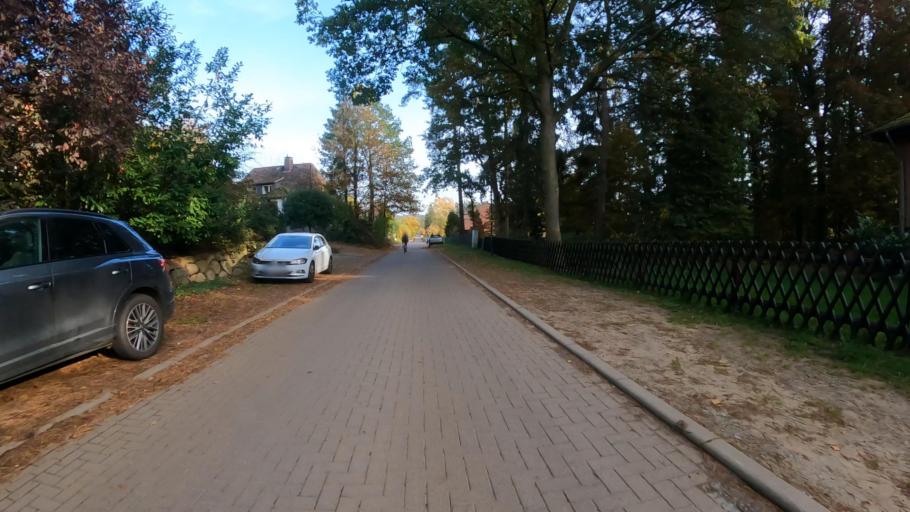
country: DE
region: Lower Saxony
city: Buchholz in der Nordheide
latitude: 53.3285
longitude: 9.8507
